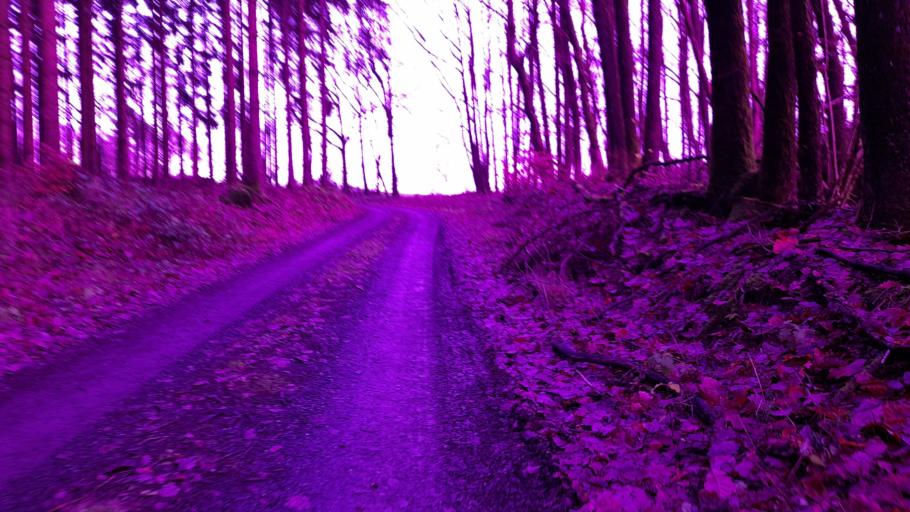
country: DE
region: Rheinland-Pfalz
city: Dasburg
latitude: 50.0853
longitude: 6.1048
